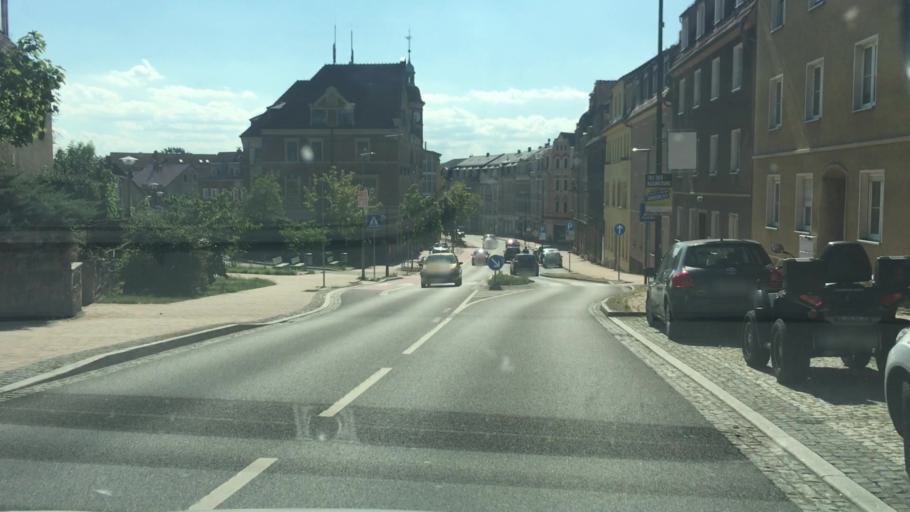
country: DE
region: Saxony
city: Pirna
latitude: 50.9717
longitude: 13.9354
